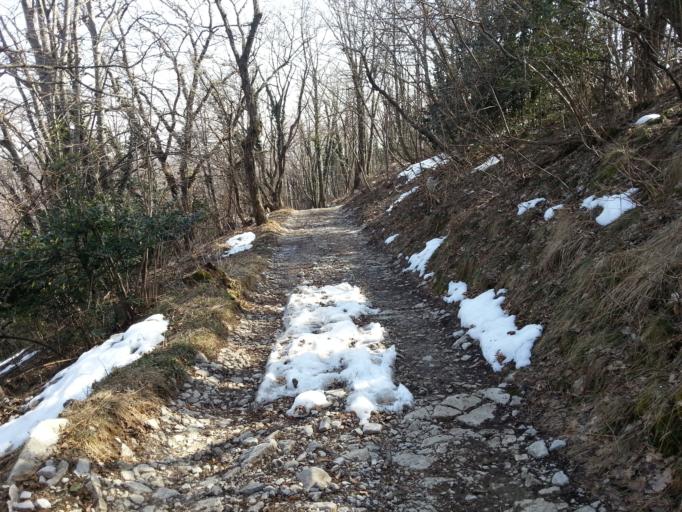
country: IT
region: Lombardy
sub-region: Provincia di Como
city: Albavilla
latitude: 45.8252
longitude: 9.1743
